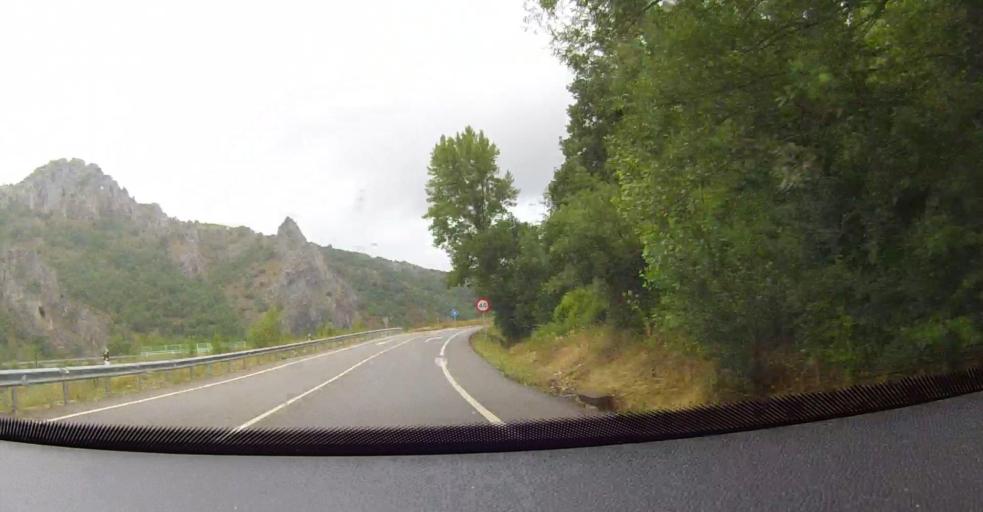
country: ES
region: Castille and Leon
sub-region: Provincia de Leon
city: Cistierna
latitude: 42.8121
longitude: -5.1312
